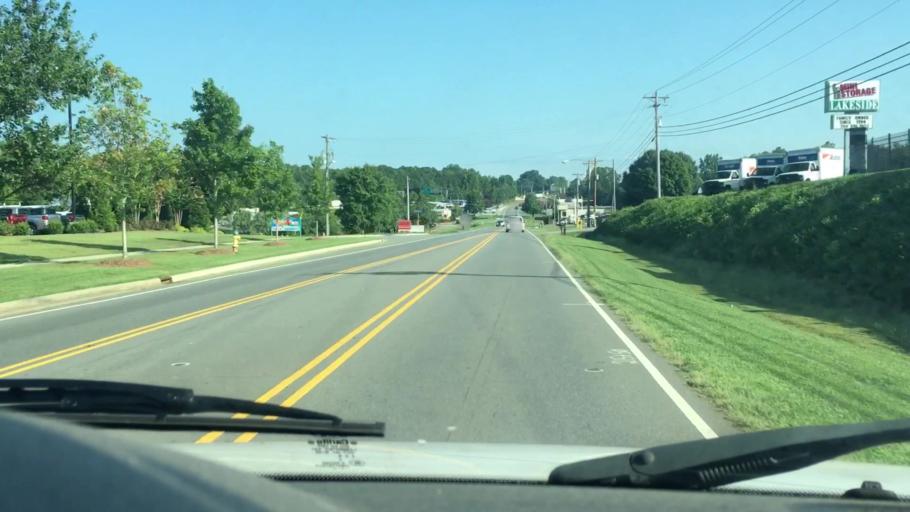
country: US
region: North Carolina
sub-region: Mecklenburg County
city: Cornelius
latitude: 35.4676
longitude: -80.8723
